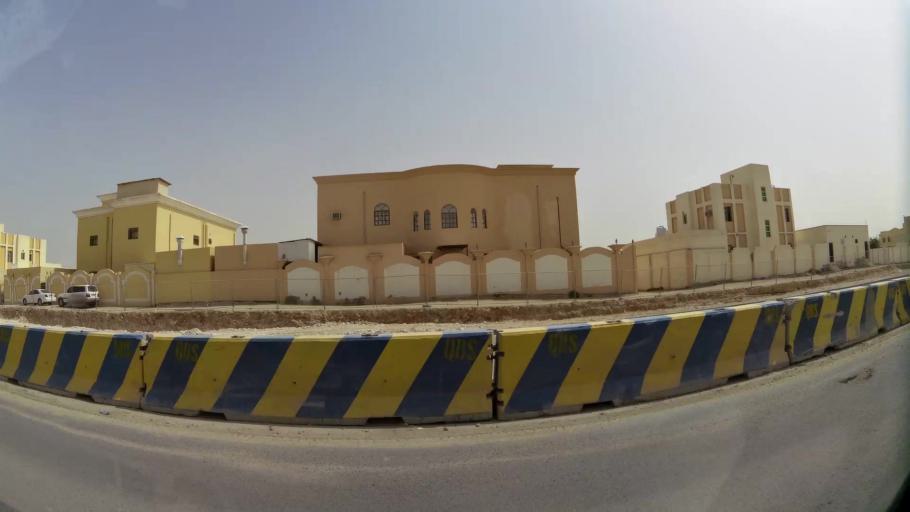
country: QA
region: Baladiyat ar Rayyan
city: Ar Rayyan
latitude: 25.2529
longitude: 51.3662
